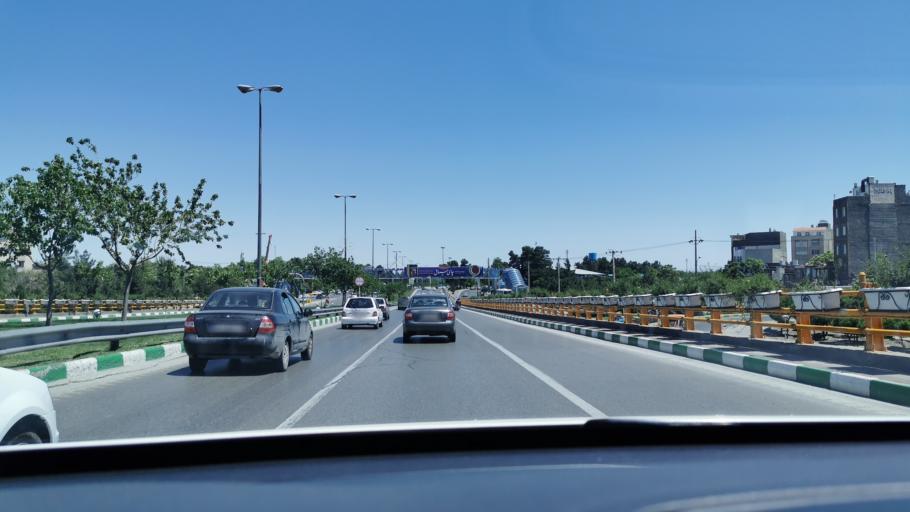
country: IR
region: Razavi Khorasan
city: Mashhad
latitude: 36.2548
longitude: 59.6009
